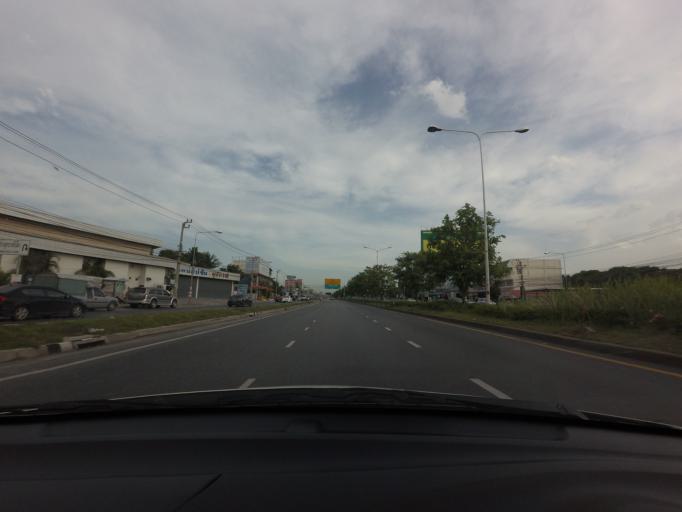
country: TH
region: Nonthaburi
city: Bang Kruai
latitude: 13.8357
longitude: 100.4472
